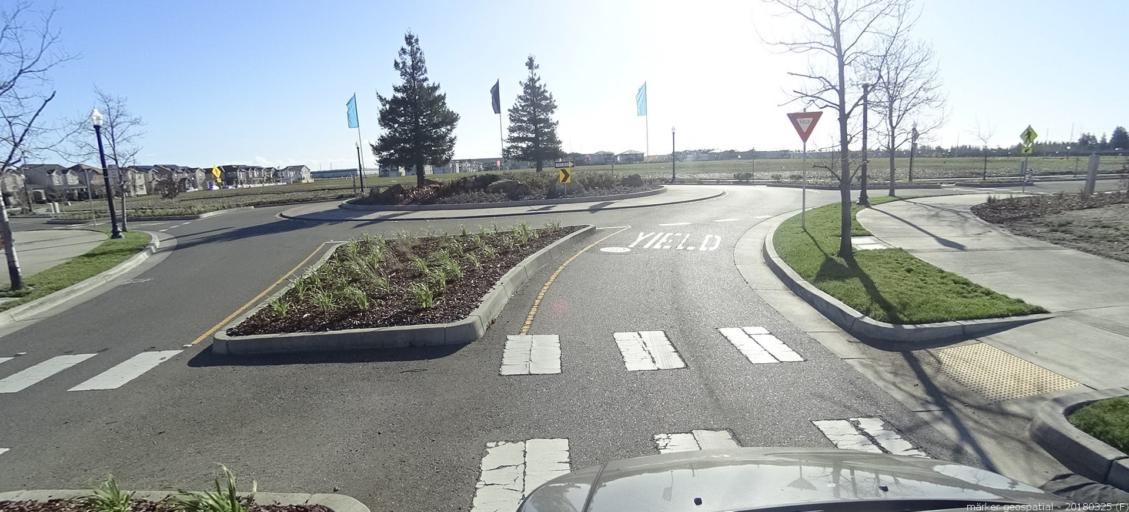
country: US
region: California
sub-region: Sacramento County
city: Rio Linda
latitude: 38.6524
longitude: -121.5005
